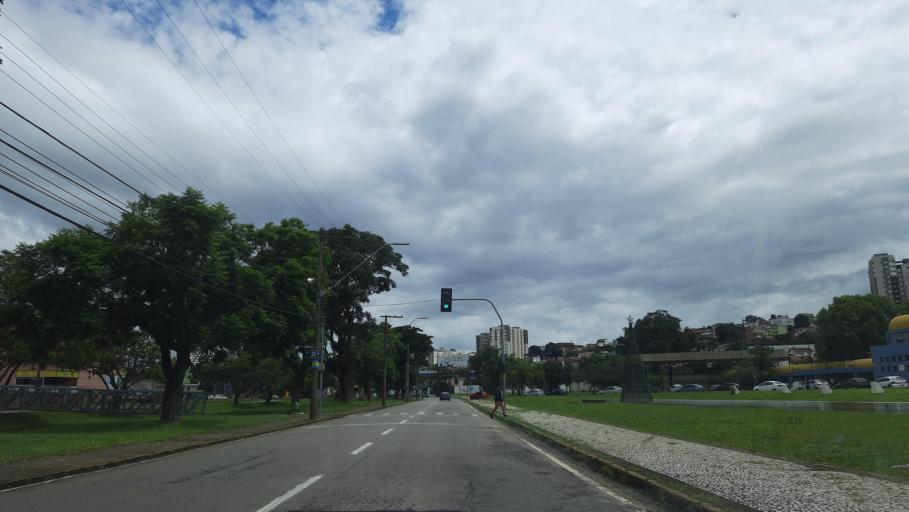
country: BR
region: Minas Gerais
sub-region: Pocos De Caldas
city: Pocos de Caldas
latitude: -21.7772
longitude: -46.6034
